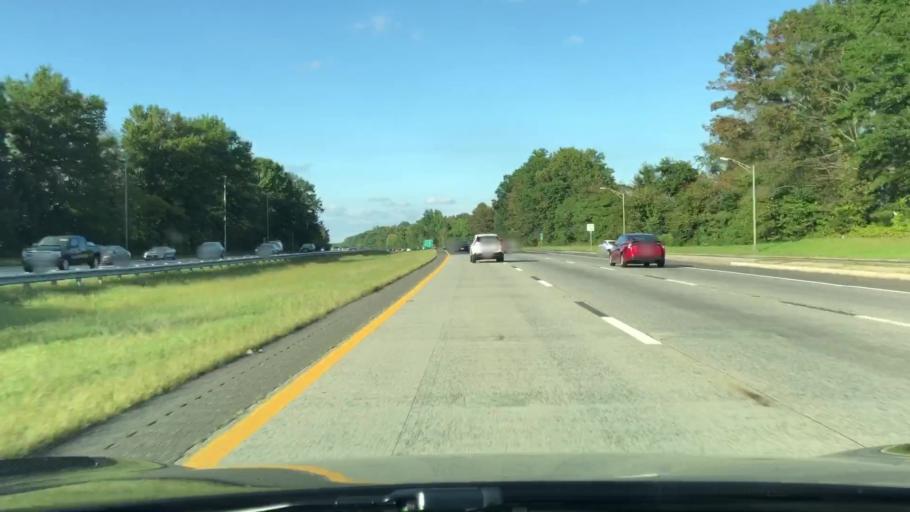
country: US
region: New Jersey
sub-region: Burlington County
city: Willingboro
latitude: 40.0116
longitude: -74.8492
